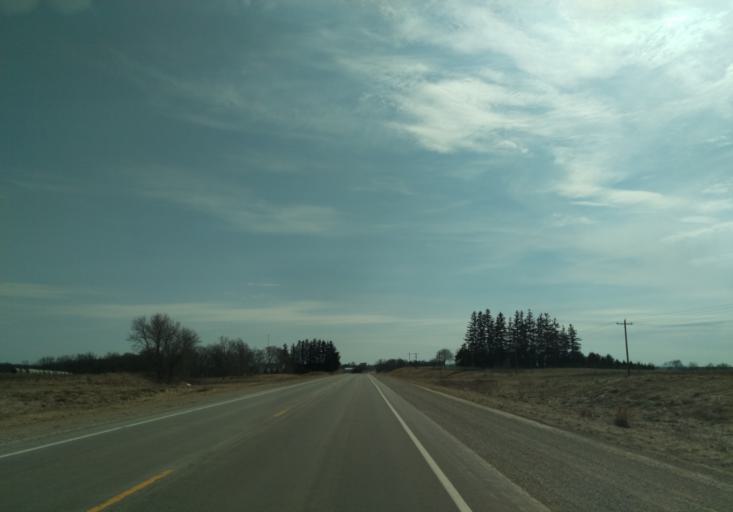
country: US
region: Iowa
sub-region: Winneshiek County
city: Decorah
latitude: 43.4353
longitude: -91.8607
